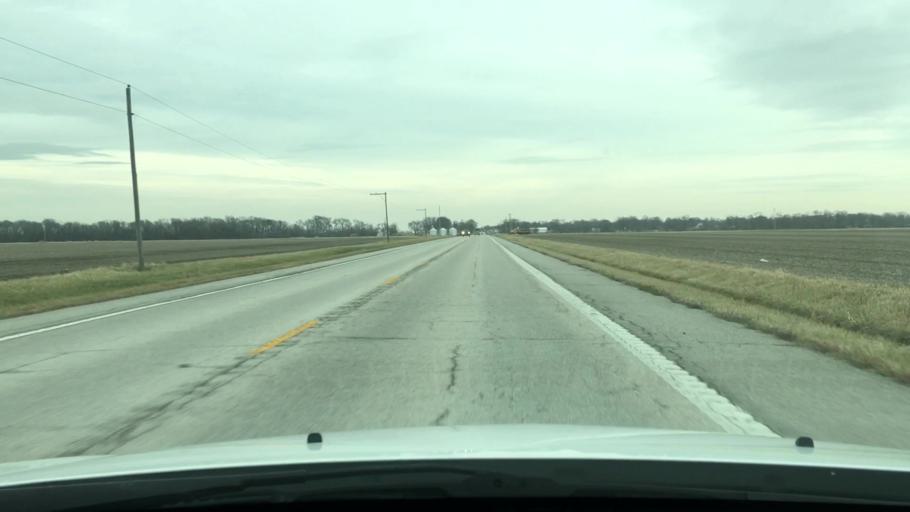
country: US
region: Missouri
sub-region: Audrain County
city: Vandalia
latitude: 39.2798
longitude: -91.5956
